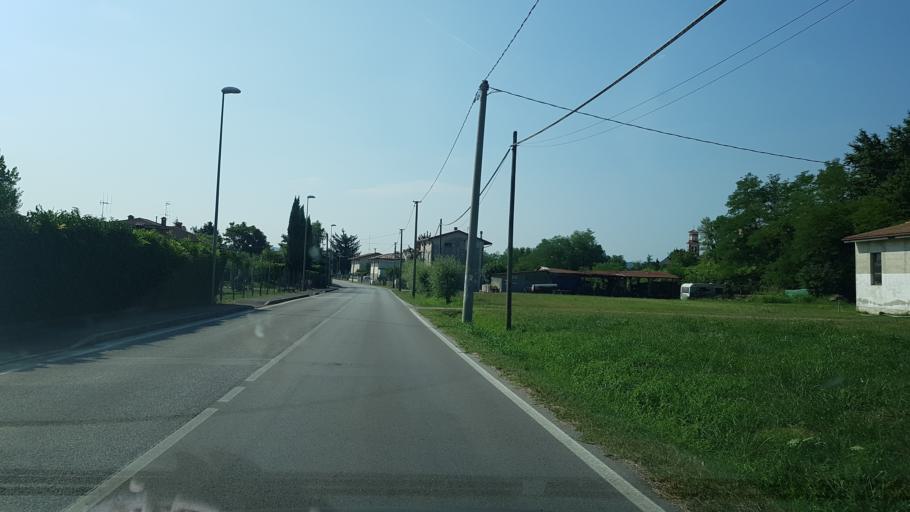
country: IT
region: Friuli Venezia Giulia
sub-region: Provincia di Gorizia
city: Mossa
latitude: 45.9415
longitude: 13.5486
